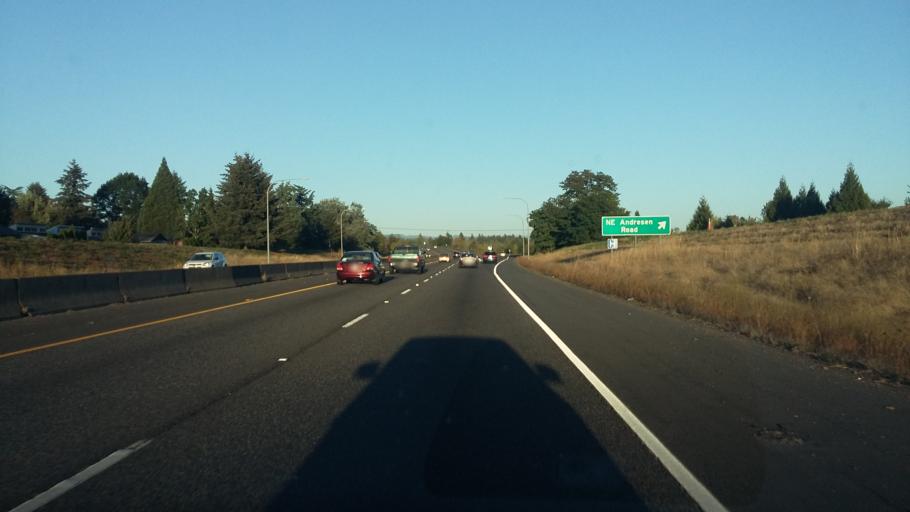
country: US
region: Washington
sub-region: Clark County
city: Walnut Grove
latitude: 45.6478
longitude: -122.6120
